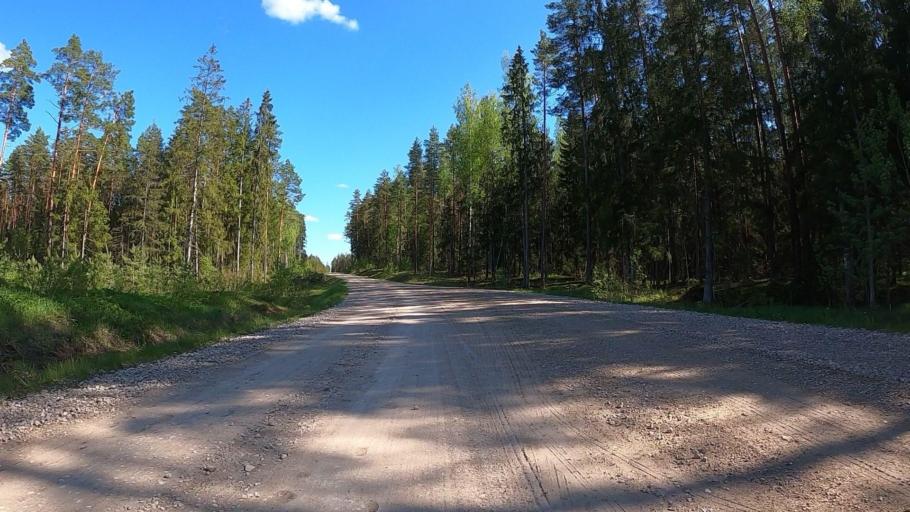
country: LV
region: Baldone
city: Baldone
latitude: 56.7698
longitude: 24.3745
